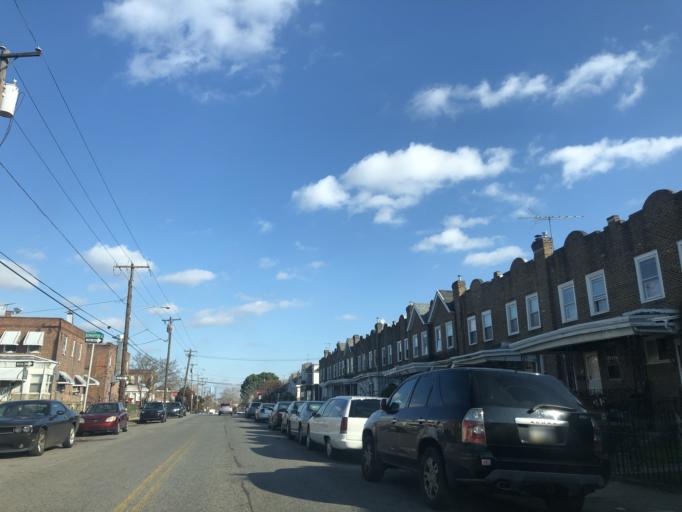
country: US
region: Pennsylvania
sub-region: Delaware County
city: Colwyn
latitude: 39.9174
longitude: -75.2310
